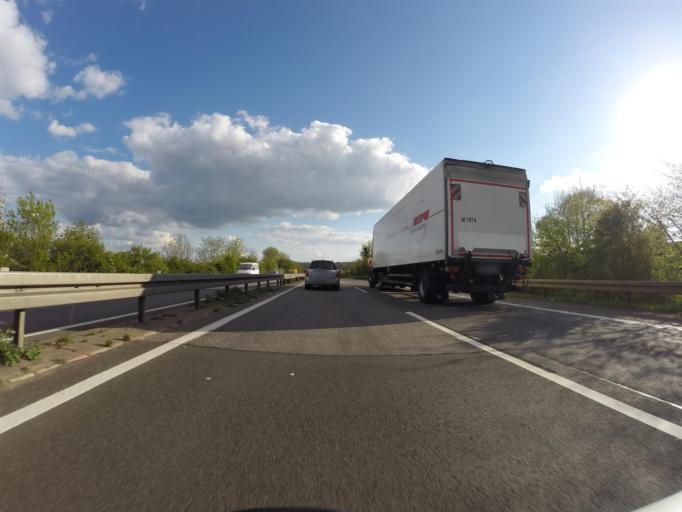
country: DE
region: Saarland
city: Wallerfangen
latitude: 49.3202
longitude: 6.7322
